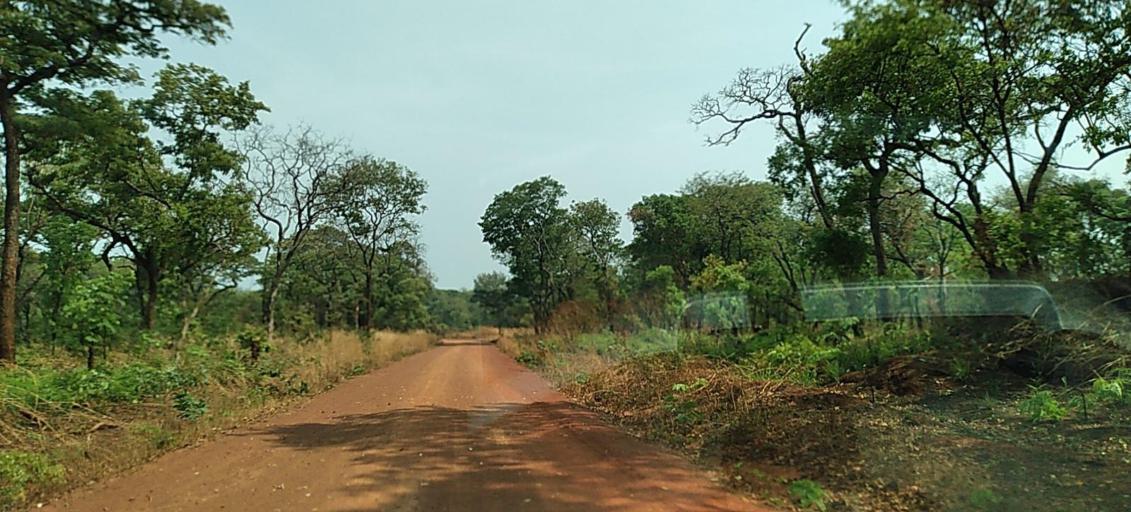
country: ZM
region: North-Western
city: Kansanshi
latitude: -11.9924
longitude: 26.8365
